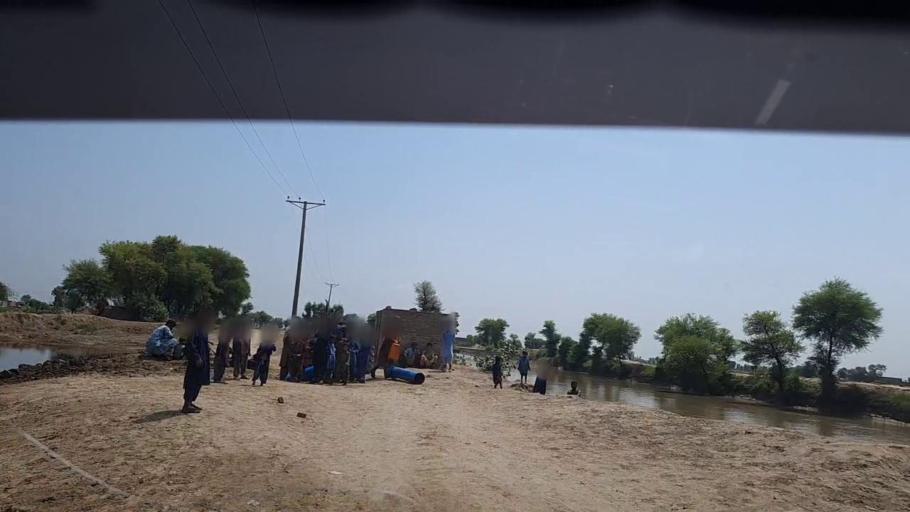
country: PK
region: Sindh
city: Tangwani
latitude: 28.2275
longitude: 68.9012
